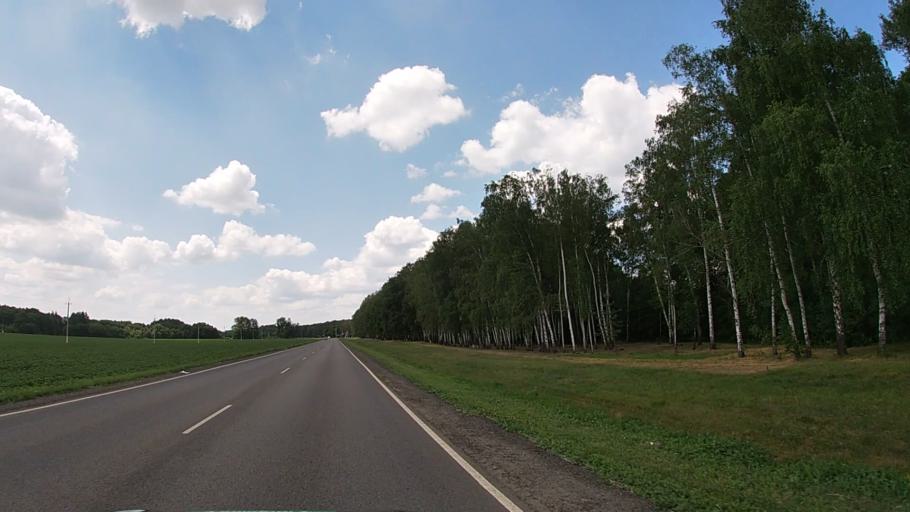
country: RU
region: Belgorod
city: Grayvoron
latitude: 50.5022
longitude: 35.7298
